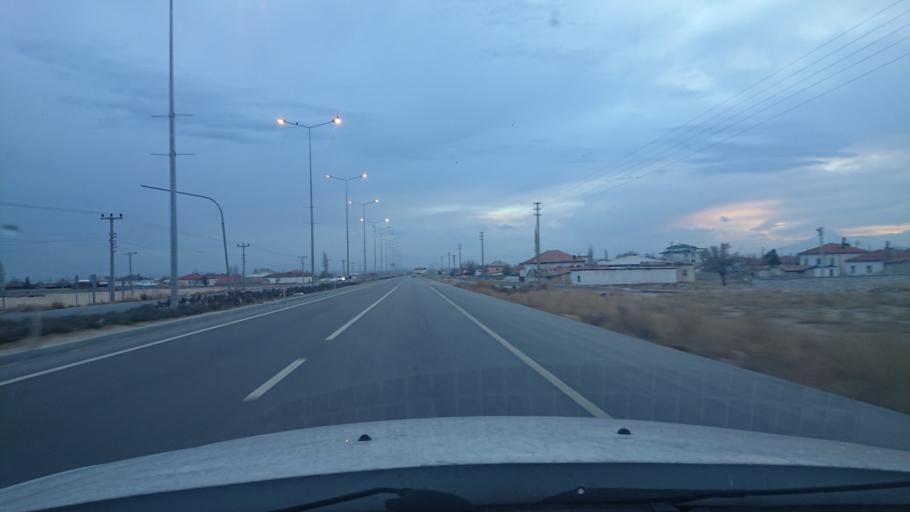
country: TR
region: Aksaray
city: Sultanhani
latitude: 38.2517
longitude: 33.5490
